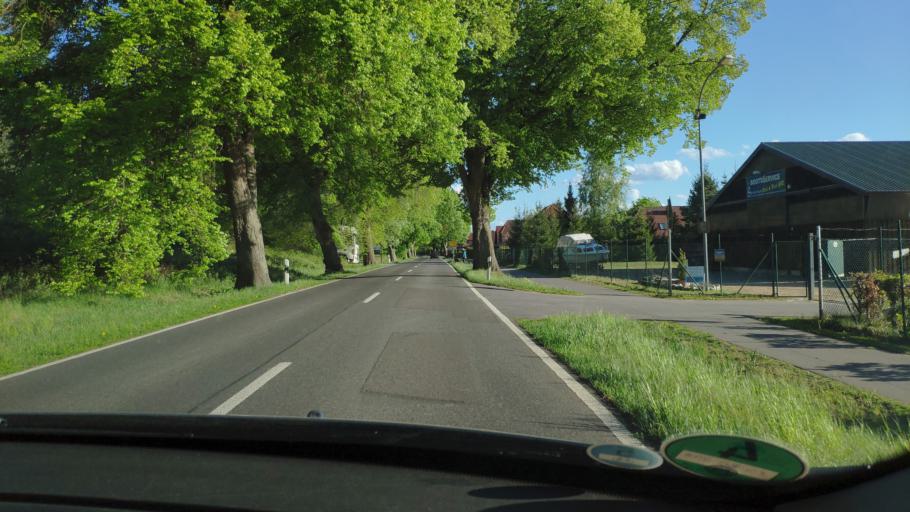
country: DE
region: Mecklenburg-Vorpommern
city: Rechlin
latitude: 53.2881
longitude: 12.8132
